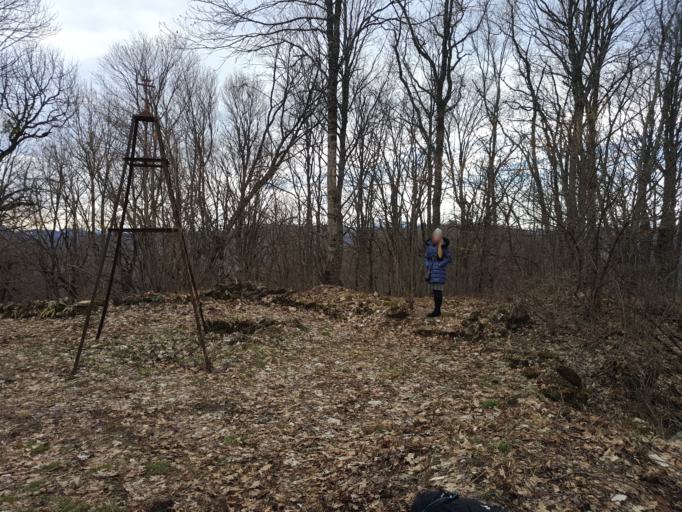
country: RU
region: Adygeya
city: Kamennomostskiy
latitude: 44.3014
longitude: 40.3259
